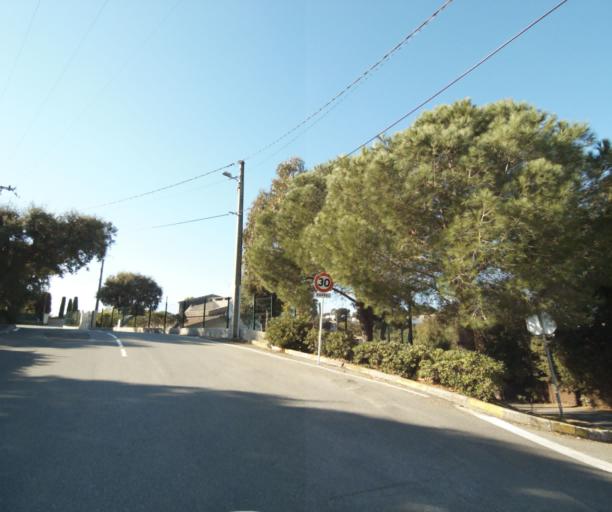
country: FR
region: Provence-Alpes-Cote d'Azur
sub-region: Departement des Alpes-Maritimes
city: Biot
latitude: 43.6051
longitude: 7.1008
